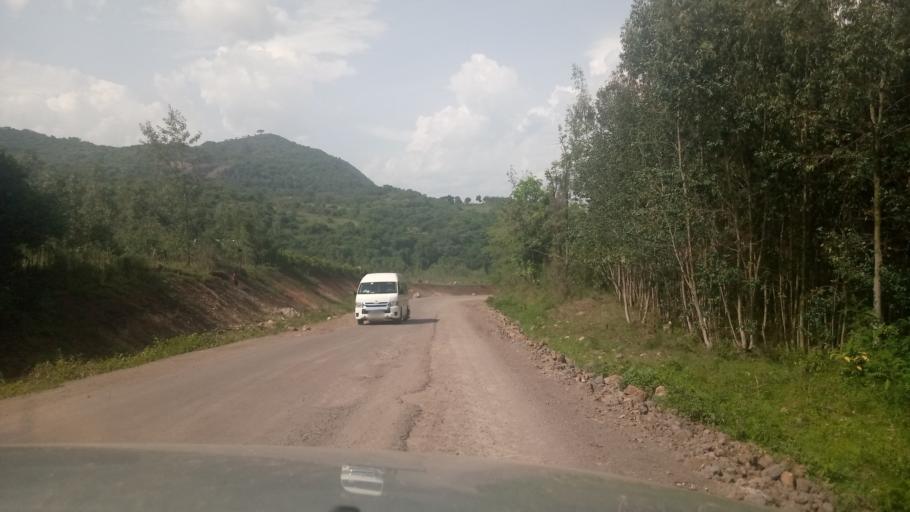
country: ET
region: Oromiya
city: Agaro
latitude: 8.0431
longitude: 36.4645
